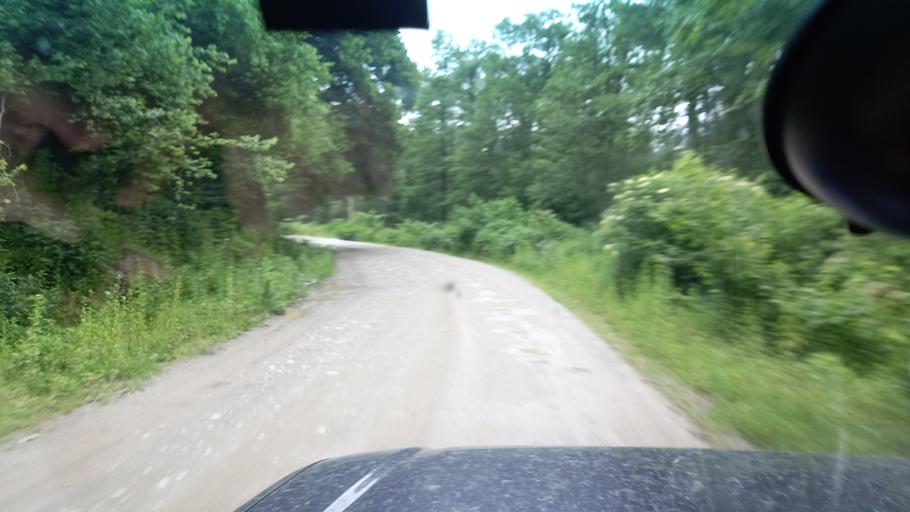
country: RU
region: Krasnodarskiy
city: Psebay
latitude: 44.0286
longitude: 40.7358
